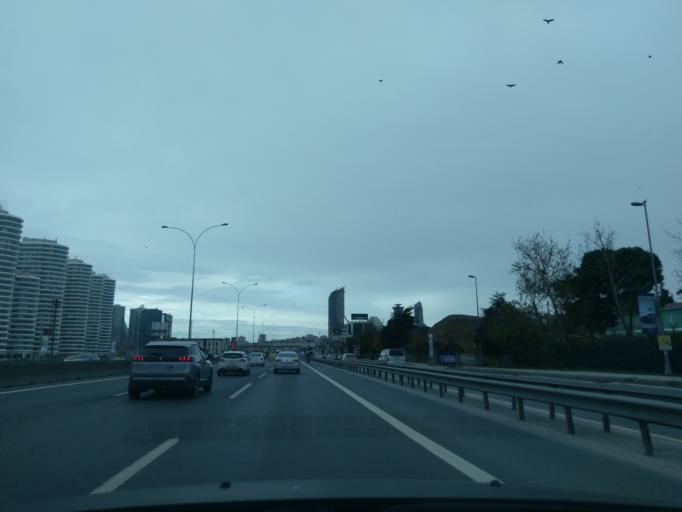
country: TR
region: Istanbul
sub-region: Atasehir
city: Atasehir
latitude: 40.9939
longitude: 29.0700
